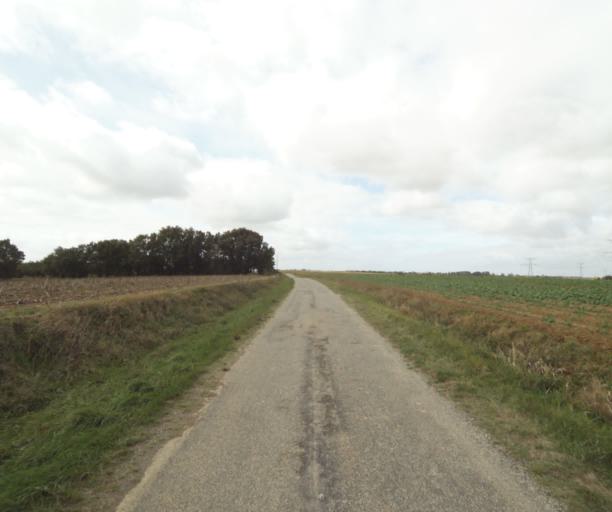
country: FR
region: Midi-Pyrenees
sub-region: Departement du Tarn-et-Garonne
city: Finhan
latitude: 43.8878
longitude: 1.1365
